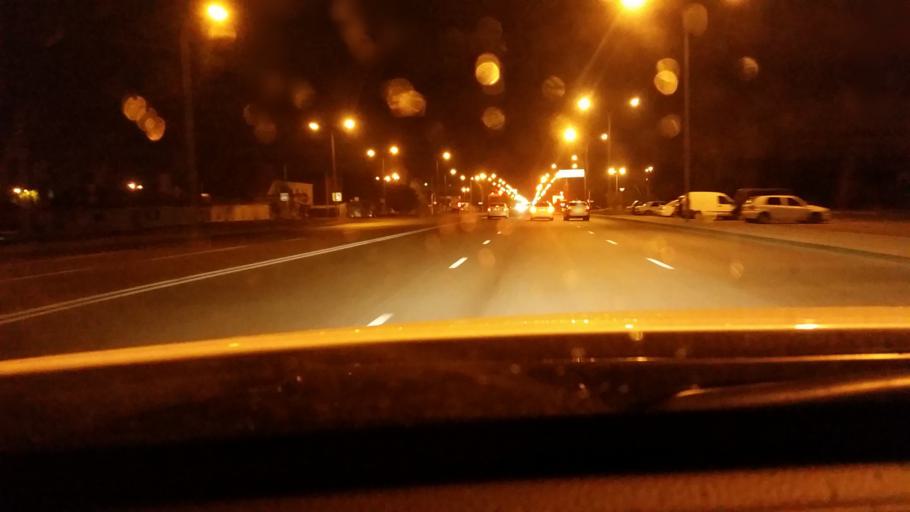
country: KZ
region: Astana Qalasy
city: Astana
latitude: 51.1407
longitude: 71.4890
